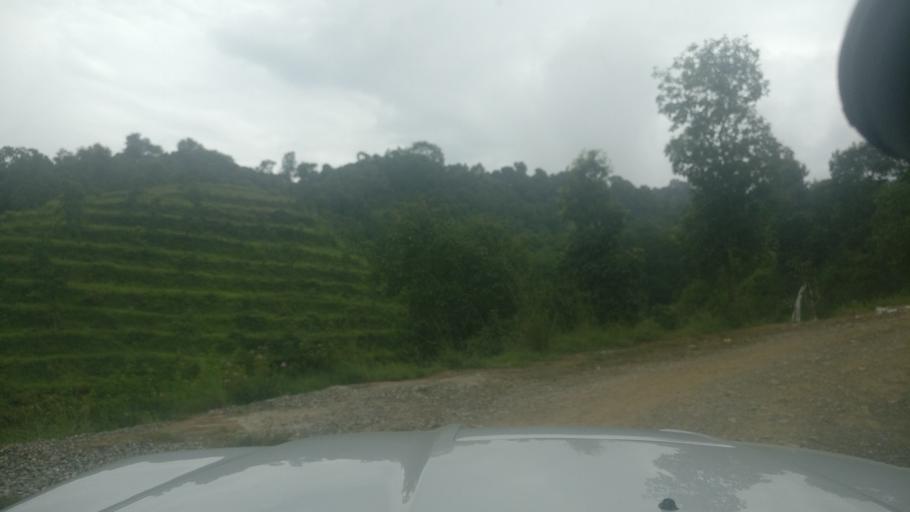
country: NP
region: Central Region
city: Kirtipur
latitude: 27.7034
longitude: 85.2545
